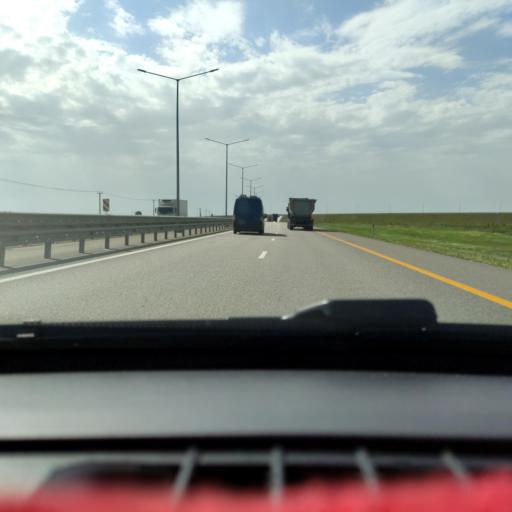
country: RU
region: Voronezj
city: Podkletnoye
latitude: 51.5106
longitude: 39.5140
